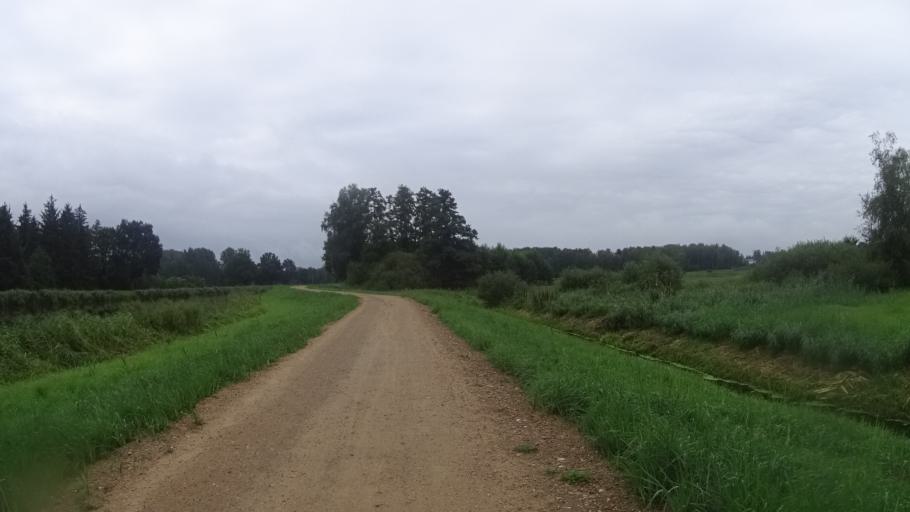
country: DE
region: Schleswig-Holstein
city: Buchen
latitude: 53.4911
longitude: 10.6296
